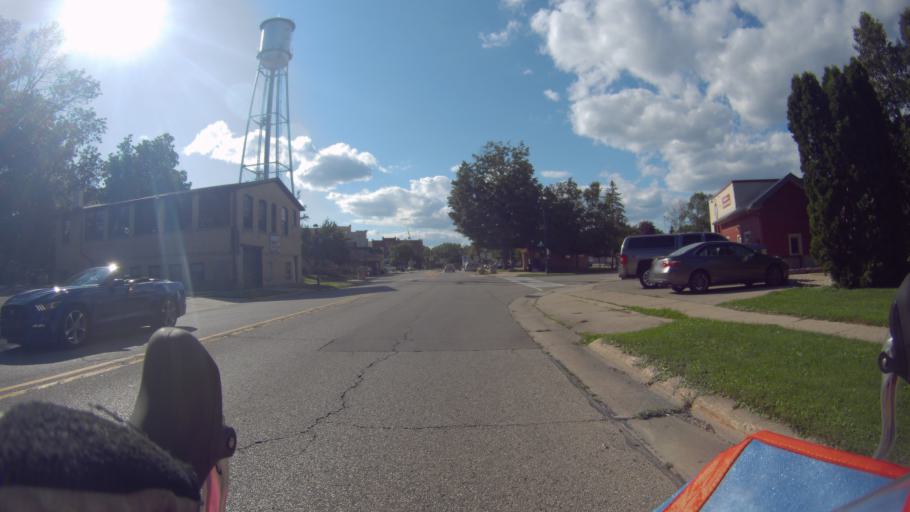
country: US
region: Wisconsin
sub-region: Dane County
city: Oregon
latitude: 42.9252
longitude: -89.3832
